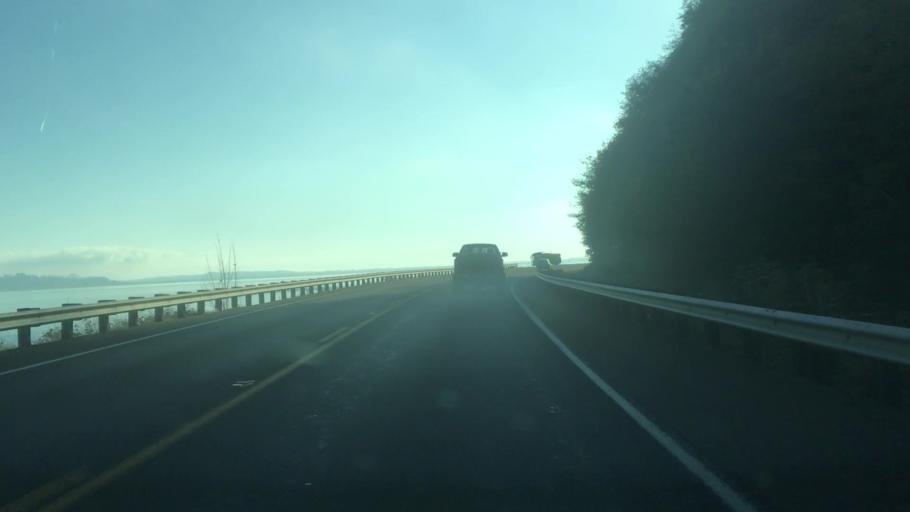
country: US
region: Oregon
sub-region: Clatsop County
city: Astoria
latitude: 46.2637
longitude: -123.8382
